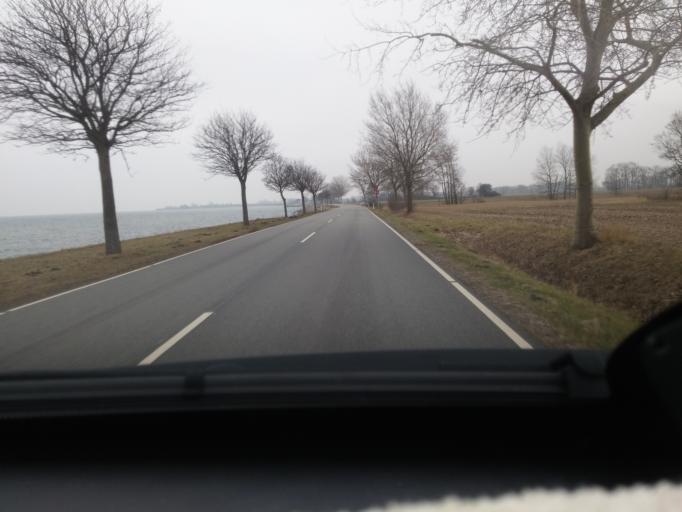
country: DK
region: South Denmark
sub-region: Kerteminde Kommune
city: Kerteminde
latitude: 55.4298
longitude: 10.6946
